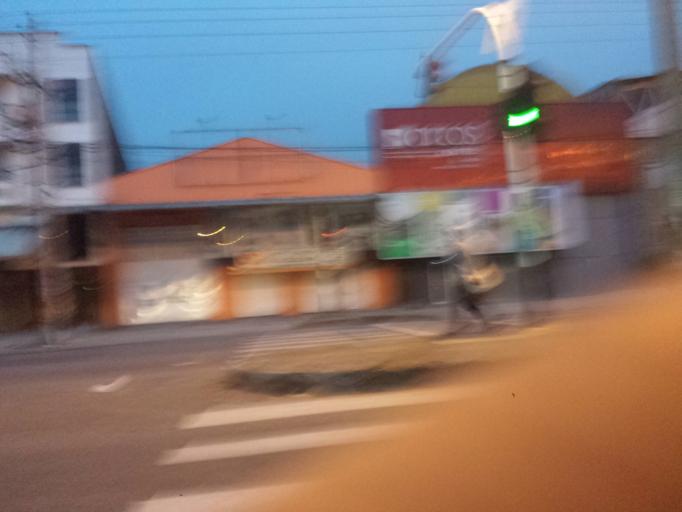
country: CO
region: Antioquia
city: Itagui
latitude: 6.1971
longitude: -75.5901
